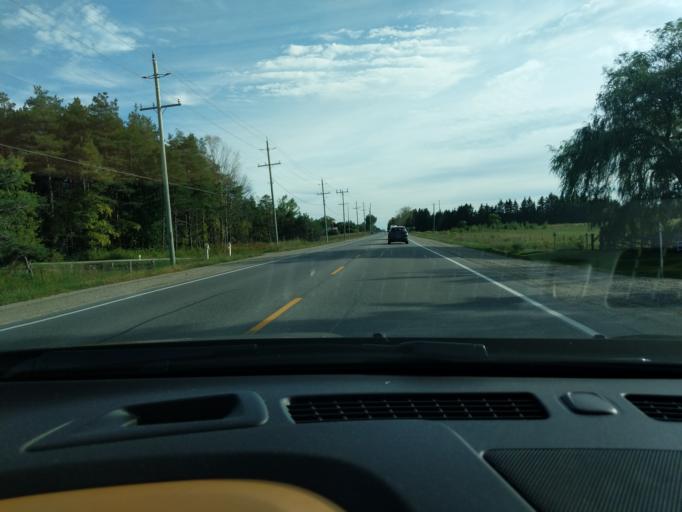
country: CA
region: Ontario
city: Wasaga Beach
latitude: 44.4379
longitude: -80.1004
